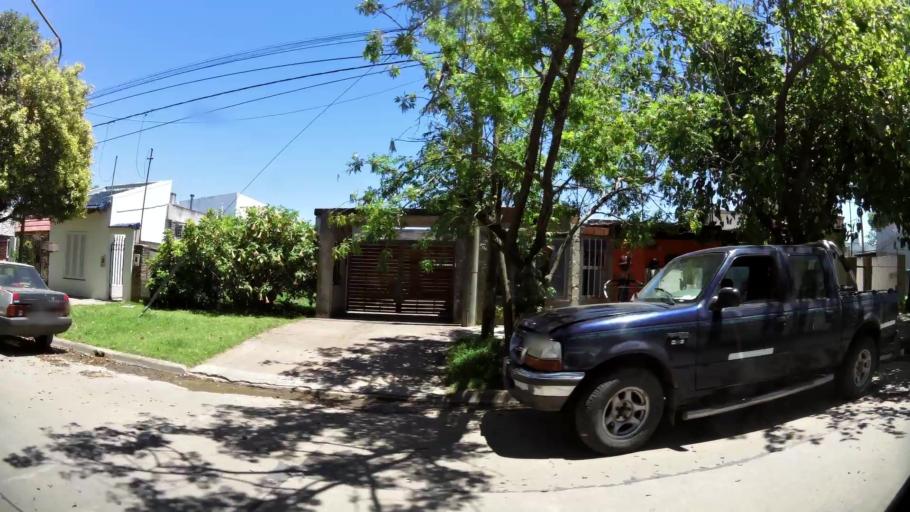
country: AR
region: Santa Fe
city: Rafaela
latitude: -31.2531
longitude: -61.4566
